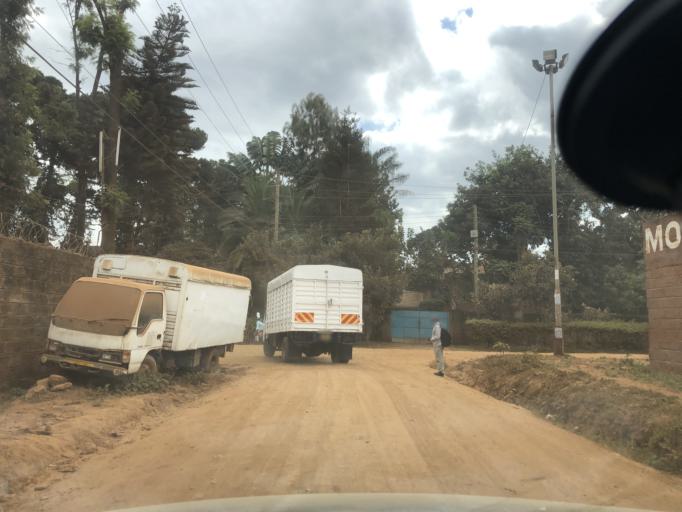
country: KE
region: Nairobi Area
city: Pumwani
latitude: -1.2312
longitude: 36.8752
